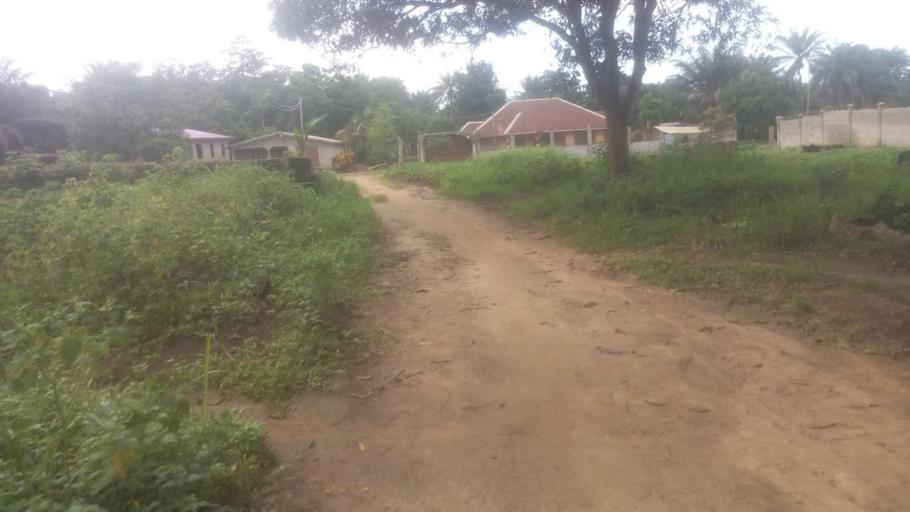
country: SL
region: Northern Province
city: Masoyila
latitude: 8.5617
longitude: -13.1645
